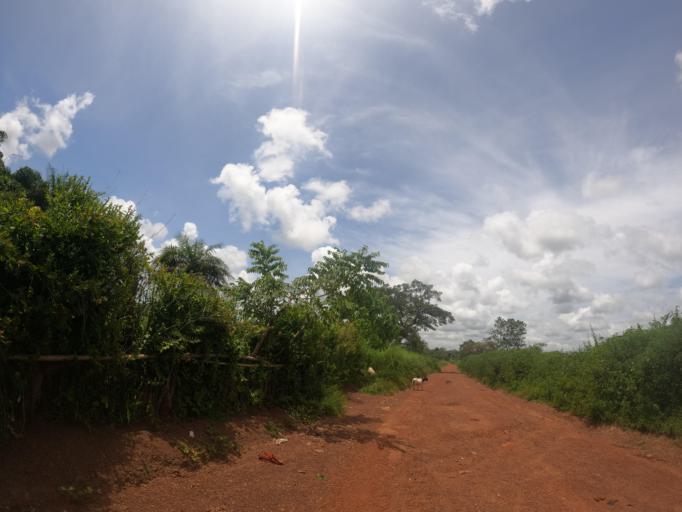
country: SL
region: Northern Province
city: Makeni
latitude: 9.1264
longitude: -12.2580
